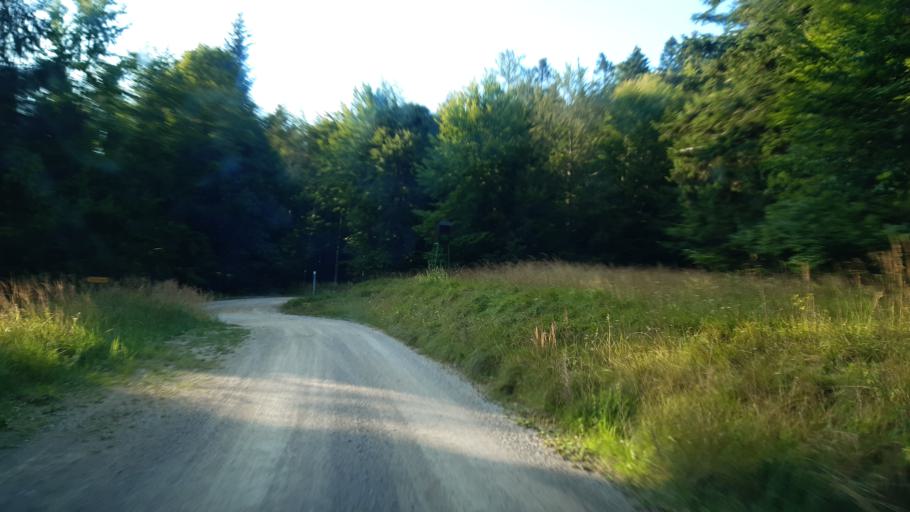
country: SI
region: Dolenjske Toplice
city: Dolenjske Toplice
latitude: 45.6745
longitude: 14.9932
